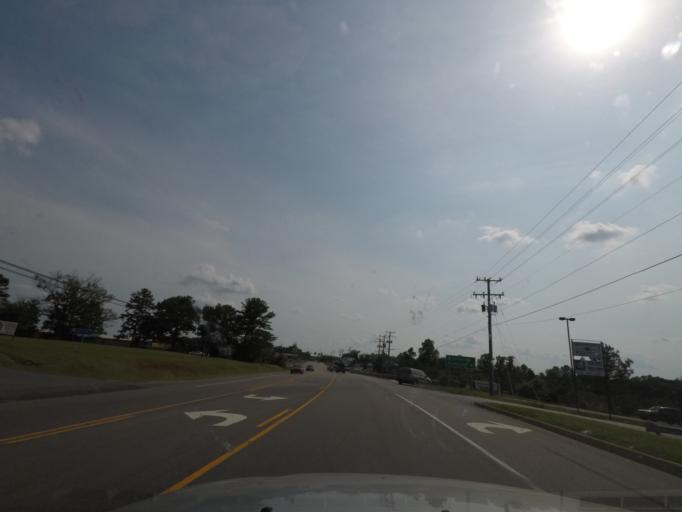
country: US
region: Virginia
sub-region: Buckingham County
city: Buckingham
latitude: 37.5447
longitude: -78.4728
